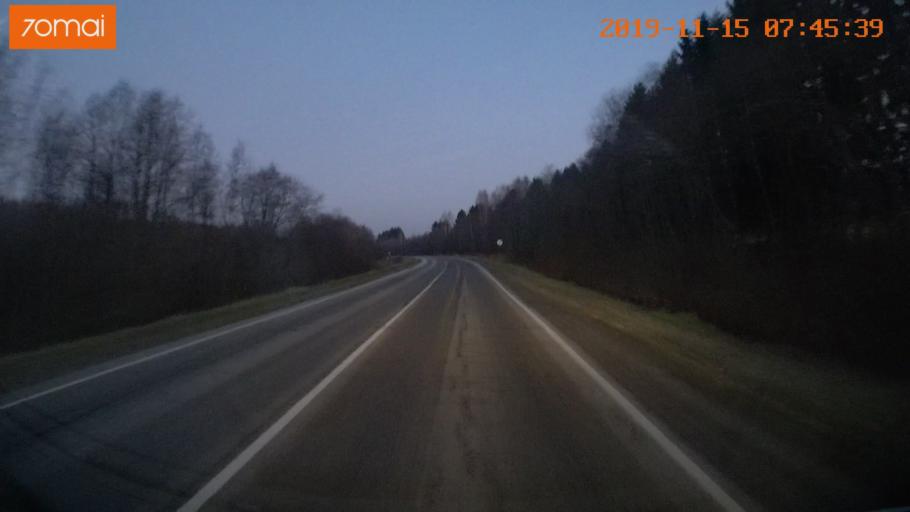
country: RU
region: Vologda
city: Sheksna
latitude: 58.8263
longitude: 38.2946
